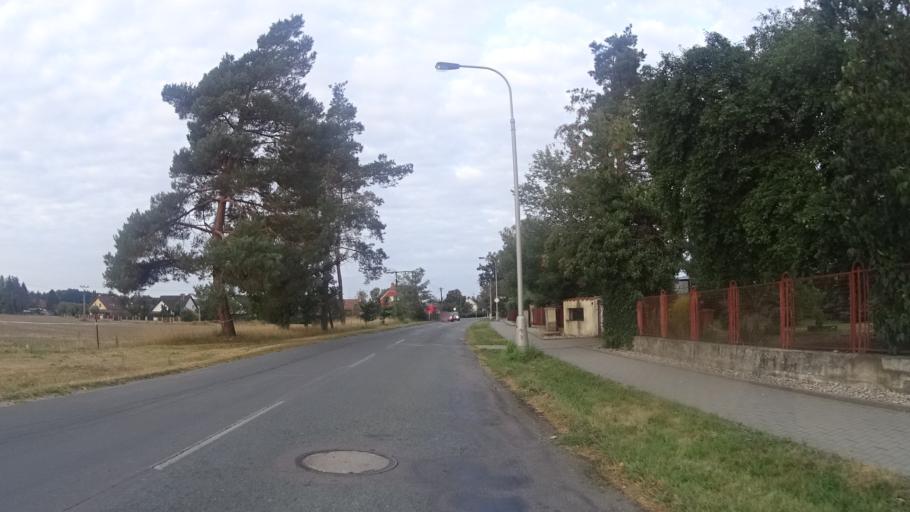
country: CZ
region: Kralovehradecky
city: Cernilov
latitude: 50.2118
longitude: 15.9063
